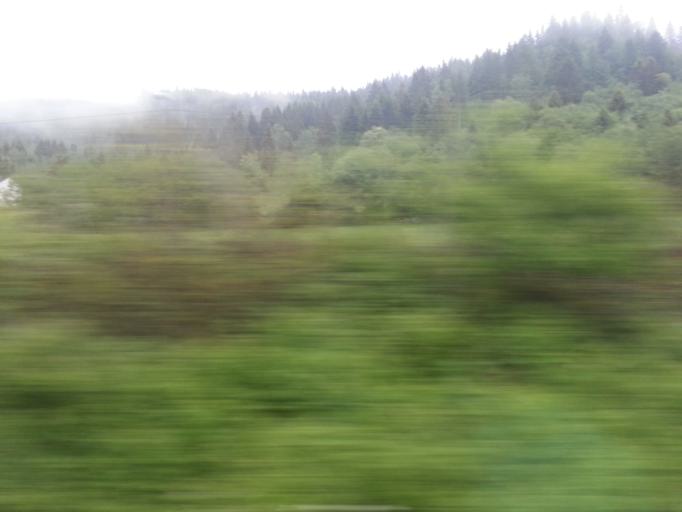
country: NO
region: Sor-Trondelag
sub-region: Melhus
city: Lundamo
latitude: 63.1197
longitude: 10.2447
